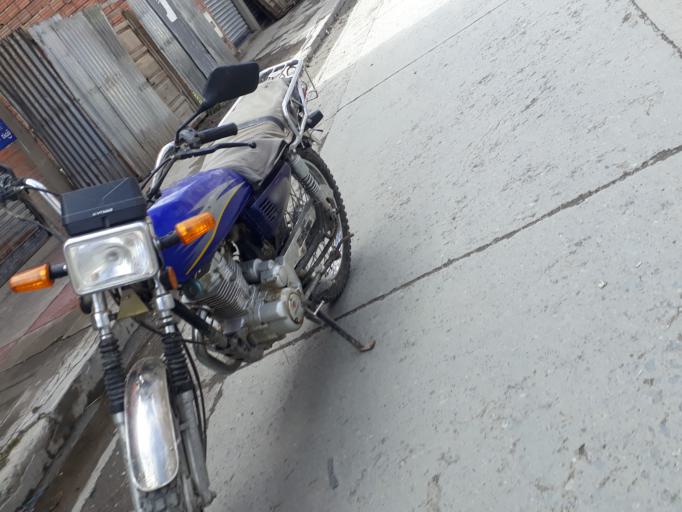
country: BO
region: La Paz
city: Achacachi
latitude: -16.0405
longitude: -68.6858
